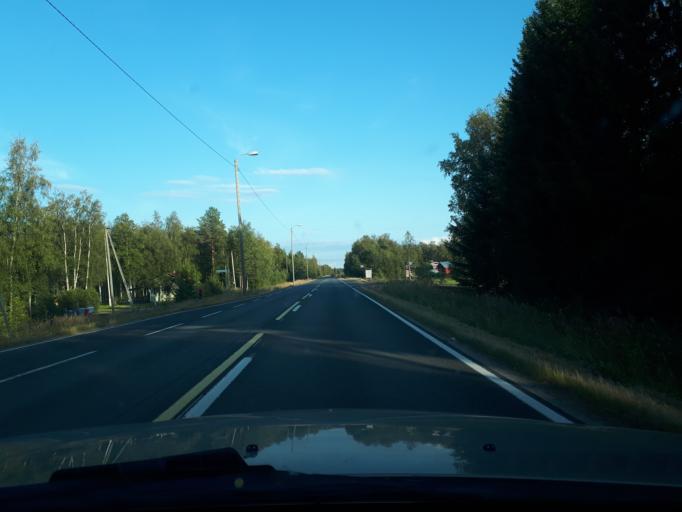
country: FI
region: Northern Ostrobothnia
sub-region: Oulu
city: Oulunsalo
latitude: 64.9860
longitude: 25.2626
